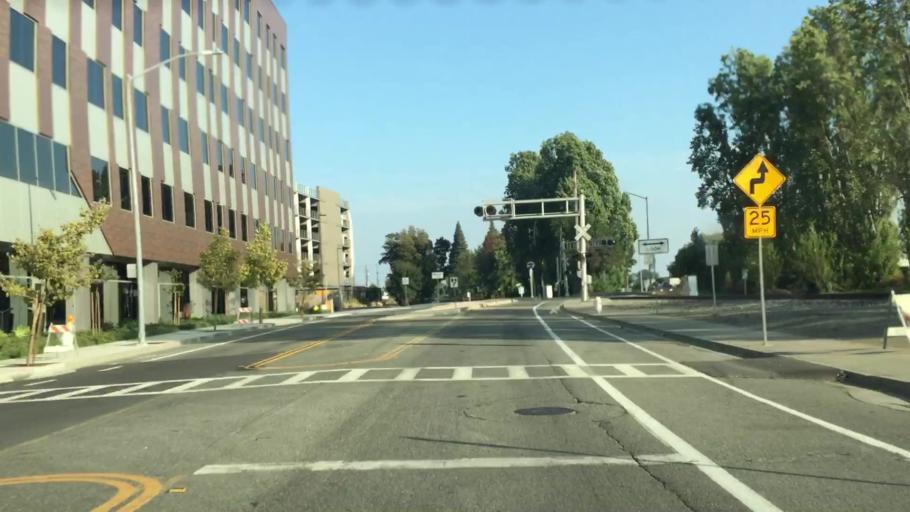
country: US
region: California
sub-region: Alameda County
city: San Leandro
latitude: 37.7212
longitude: -122.1624
